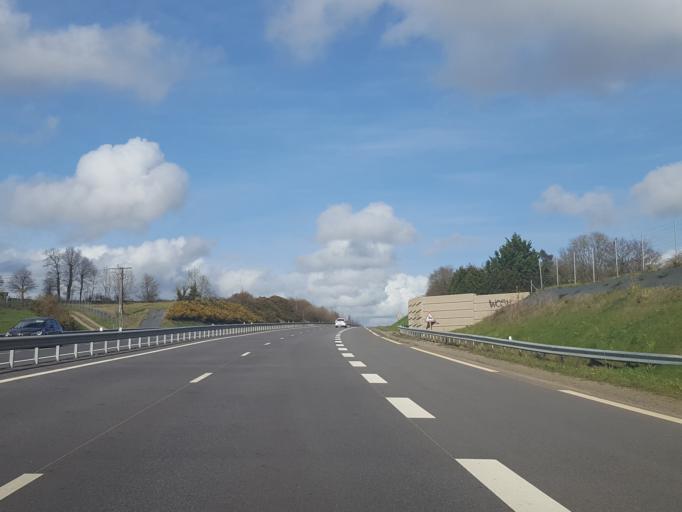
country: FR
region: Brittany
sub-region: Departement d'Ille-et-Vilaine
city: Guichen
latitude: 47.9466
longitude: -1.8251
